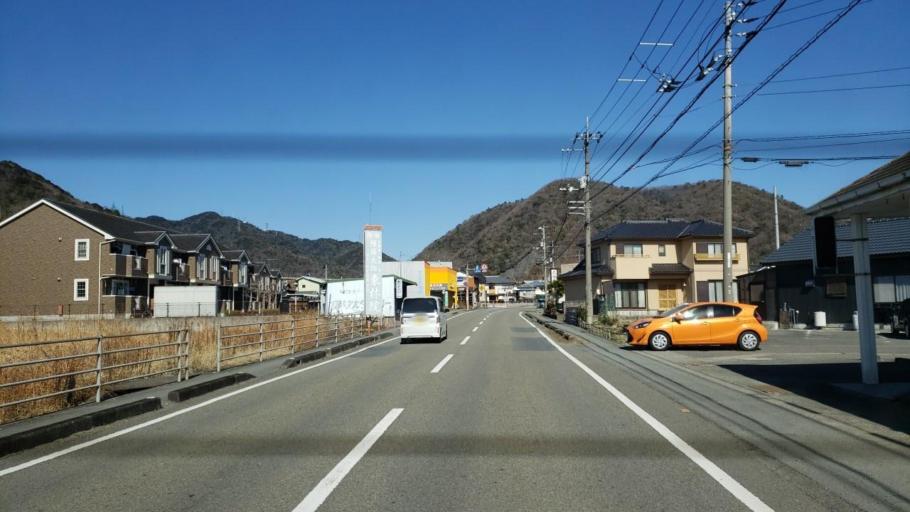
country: JP
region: Tokushima
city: Narutocho-mitsuishi
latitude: 34.1601
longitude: 134.5378
